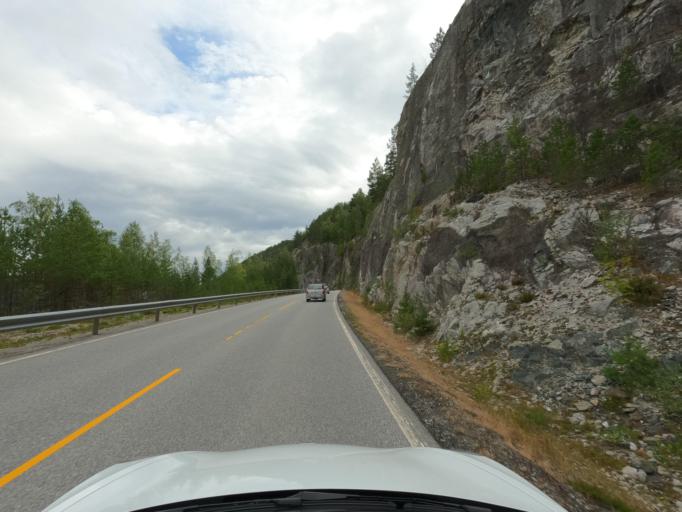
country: NO
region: Telemark
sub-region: Hjartdal
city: Sauland
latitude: 59.7813
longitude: 9.0083
